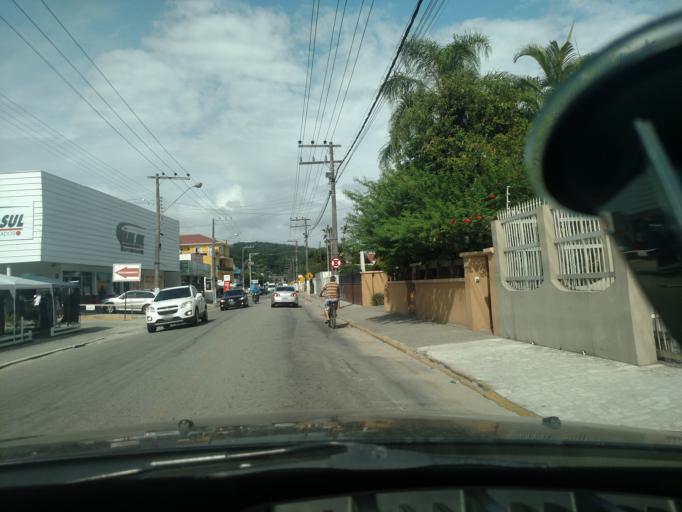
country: BR
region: Santa Catarina
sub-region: Porto Belo
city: Porto Belo
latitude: -27.1552
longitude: -48.5441
